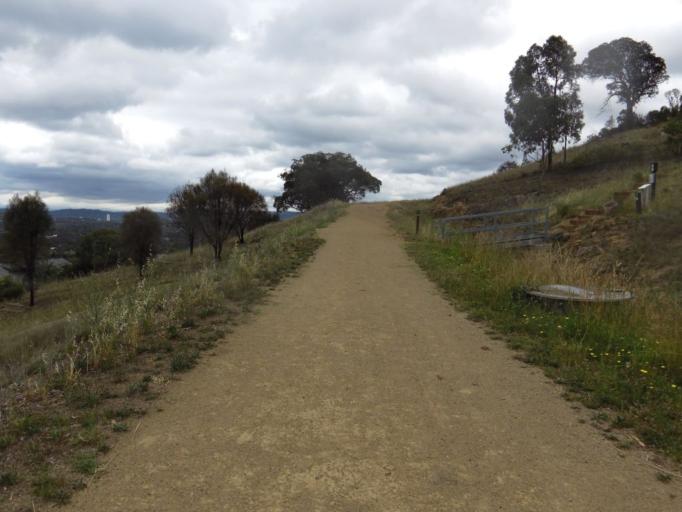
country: AU
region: Australian Capital Territory
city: Forrest
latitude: -35.3538
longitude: 149.0295
